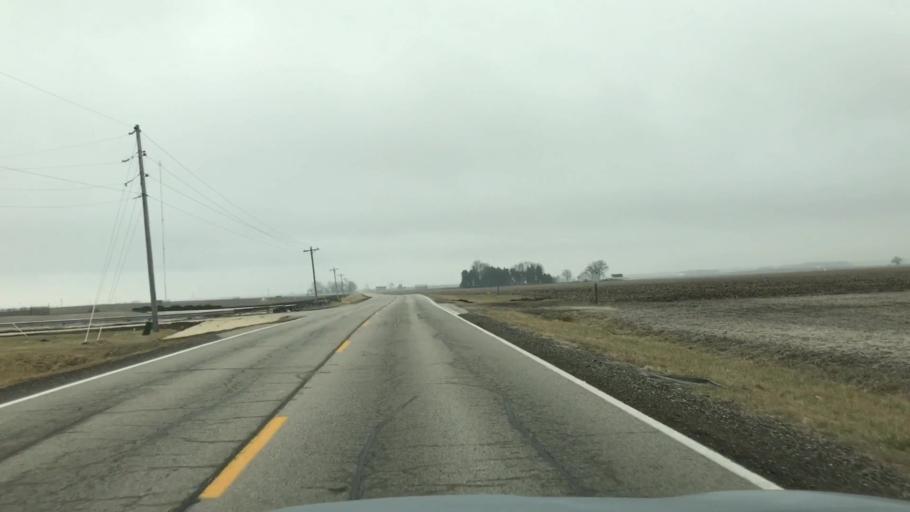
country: US
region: Illinois
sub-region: McLean County
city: Hudson
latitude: 40.5842
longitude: -88.9448
